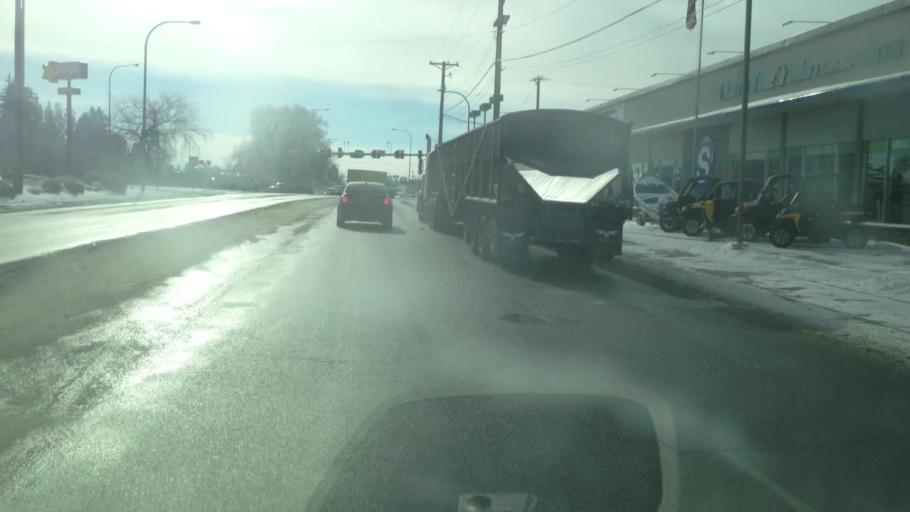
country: US
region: Idaho
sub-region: Bonneville County
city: Idaho Falls
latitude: 43.5077
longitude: -112.0238
